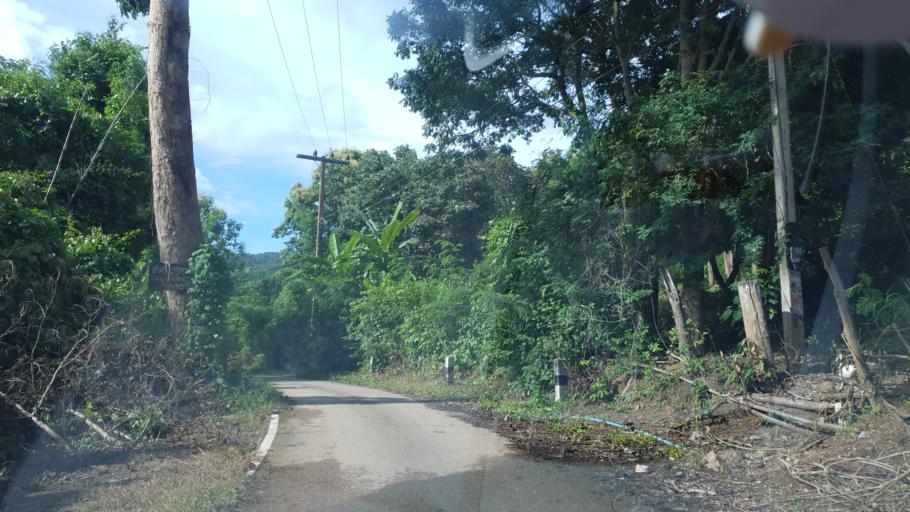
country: TH
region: Mae Hong Son
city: Khun Yuam
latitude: 18.6511
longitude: 97.9429
